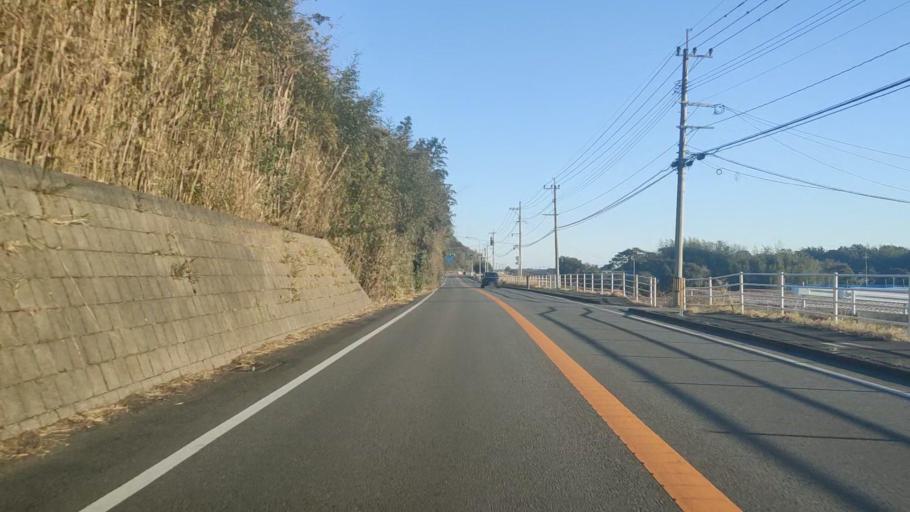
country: JP
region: Miyazaki
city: Takanabe
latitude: 32.1019
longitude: 131.5210
